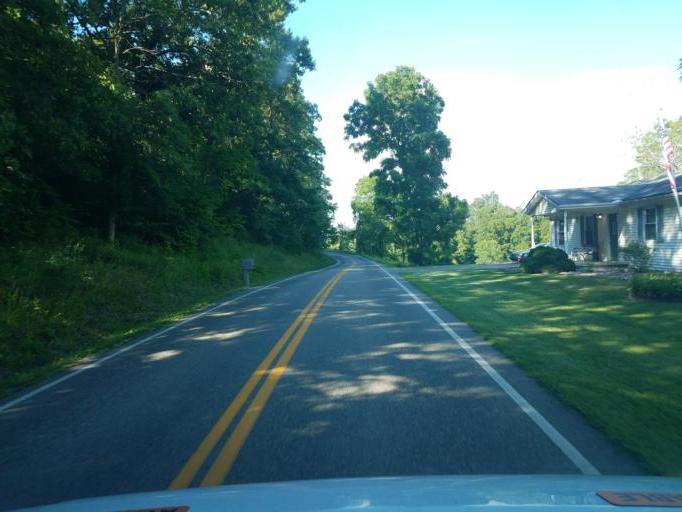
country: US
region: Ohio
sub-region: Gallia County
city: Gallipolis
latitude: 38.7839
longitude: -82.3452
